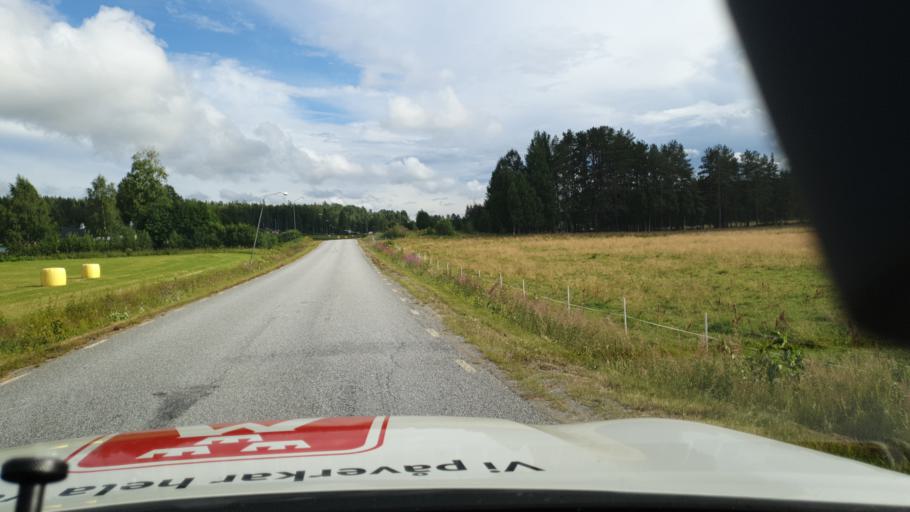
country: SE
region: Vaesterbotten
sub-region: Skelleftea Kommun
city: Burea
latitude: 64.5020
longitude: 21.0136
